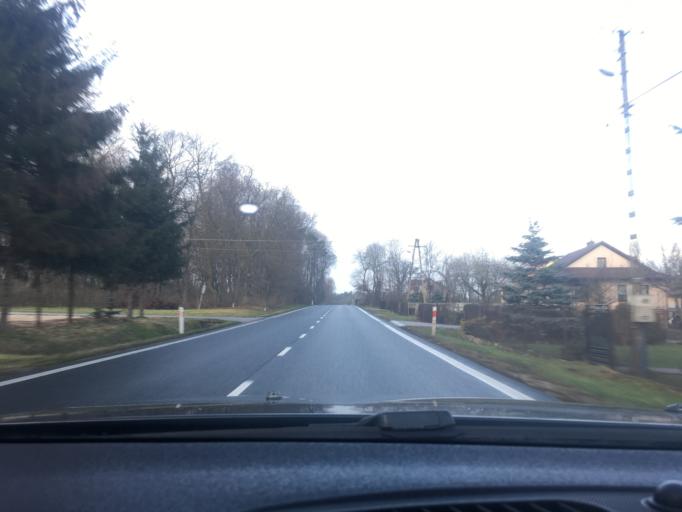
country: PL
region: Swietokrzyskie
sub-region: Powiat jedrzejowski
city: Imielno
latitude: 50.6227
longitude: 20.3969
